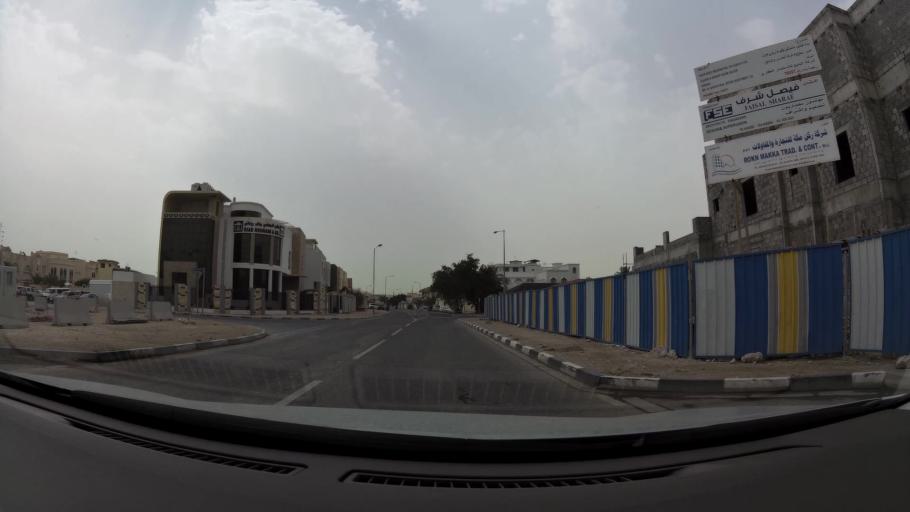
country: QA
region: Baladiyat ad Dawhah
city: Doha
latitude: 25.2620
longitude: 51.5420
